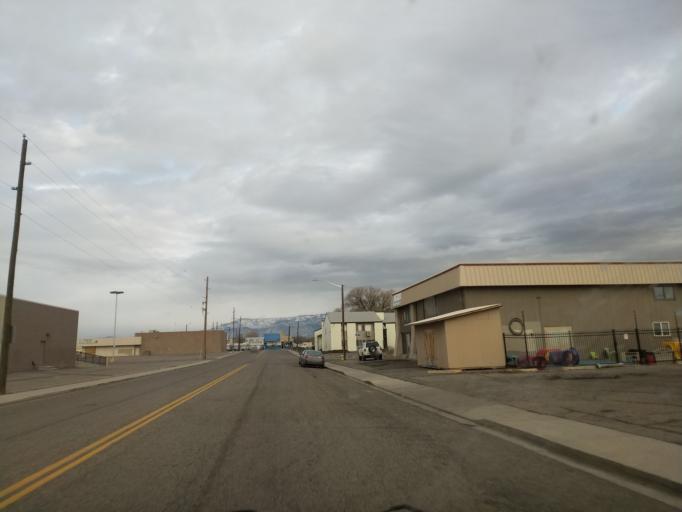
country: US
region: Colorado
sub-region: Mesa County
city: Grand Junction
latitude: 39.0755
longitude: -108.5360
